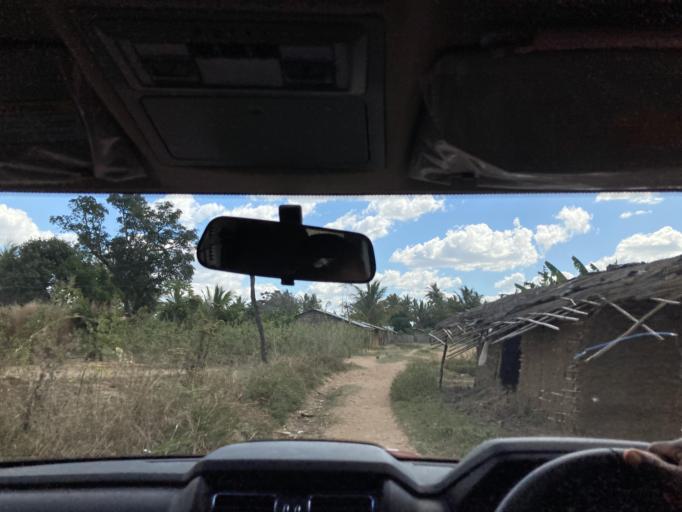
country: MZ
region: Cabo Delgado
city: Montepuez
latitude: -13.1454
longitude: 38.9991
